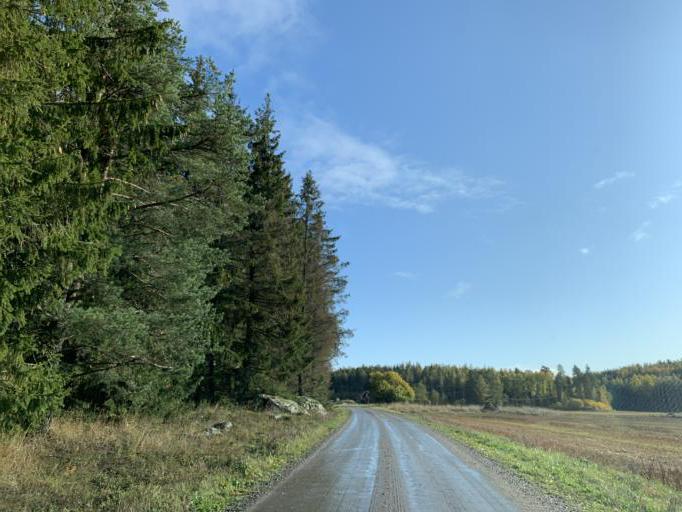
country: SE
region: Soedermanland
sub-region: Eskilstuna Kommun
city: Kvicksund
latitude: 59.3764
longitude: 16.2627
